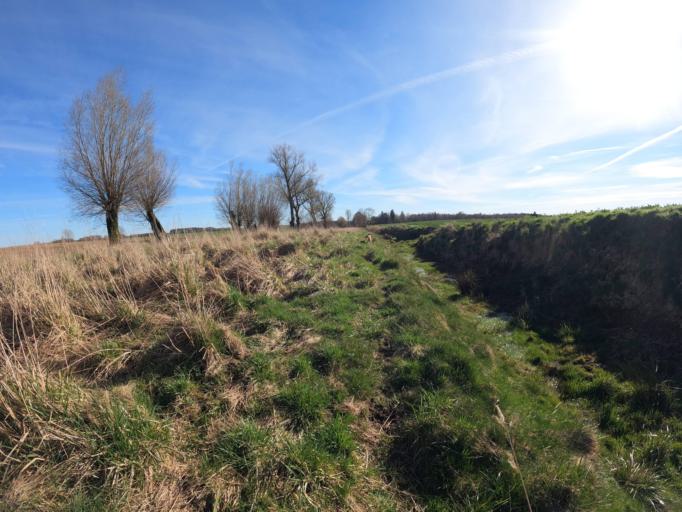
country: PL
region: West Pomeranian Voivodeship
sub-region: Powiat gryficki
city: Brojce
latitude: 53.9177
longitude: 15.3239
